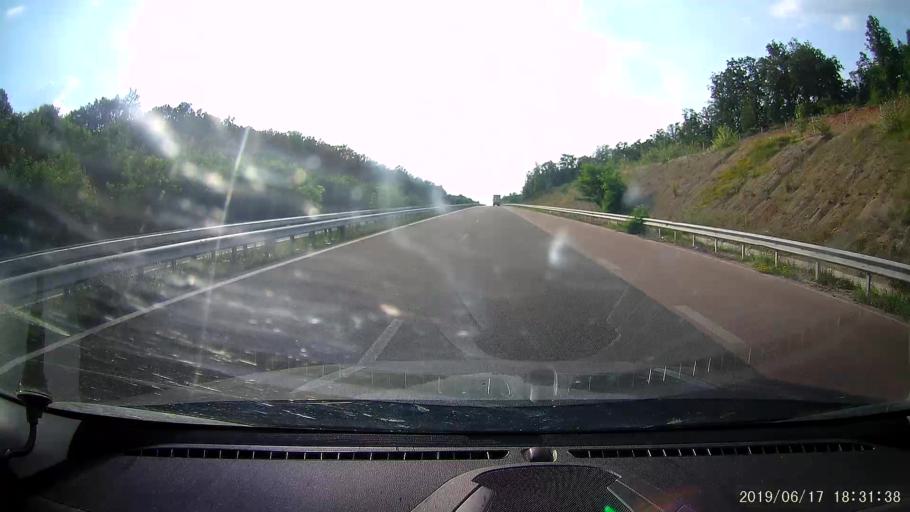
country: BG
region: Khaskovo
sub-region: Obshtina Dimitrovgrad
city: Dimitrovgrad
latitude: 42.0490
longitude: 25.4991
